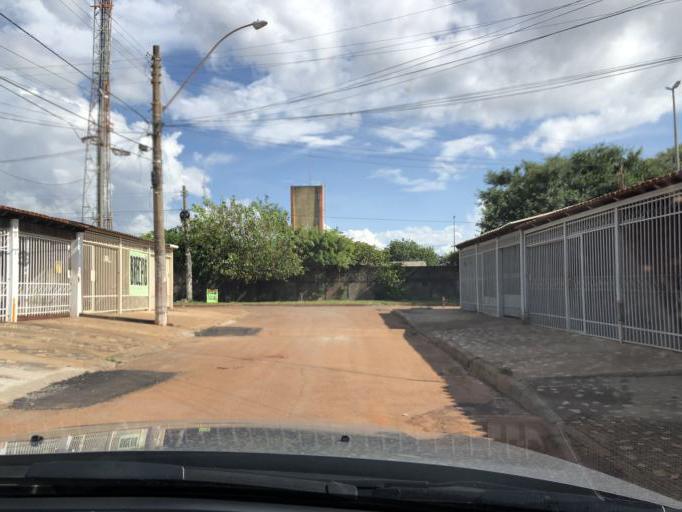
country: BR
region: Federal District
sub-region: Brasilia
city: Brasilia
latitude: -15.7963
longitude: -48.1223
